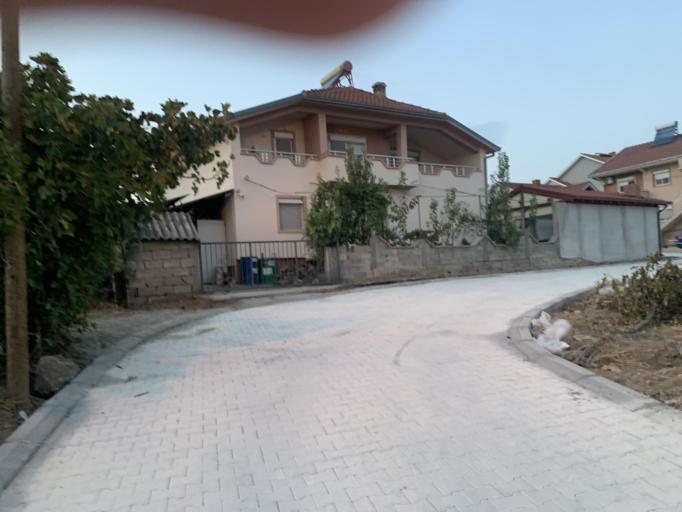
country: MK
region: Bogdanci
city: Bogdanci
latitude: 41.2035
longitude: 22.5675
